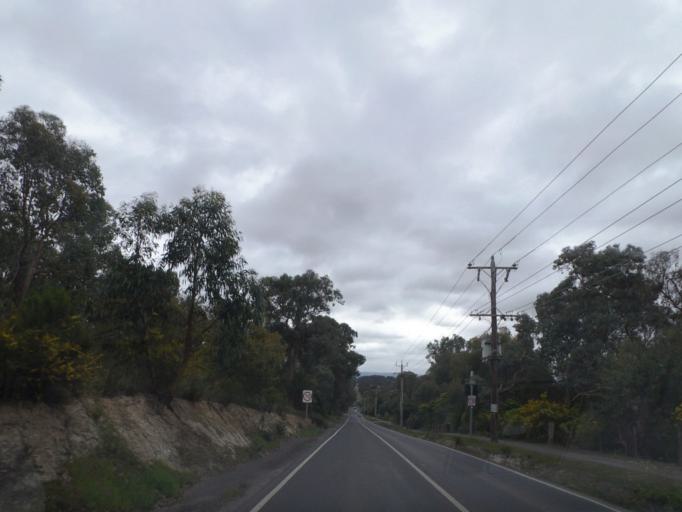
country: AU
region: Victoria
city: Plenty
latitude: -37.6384
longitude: 145.1325
